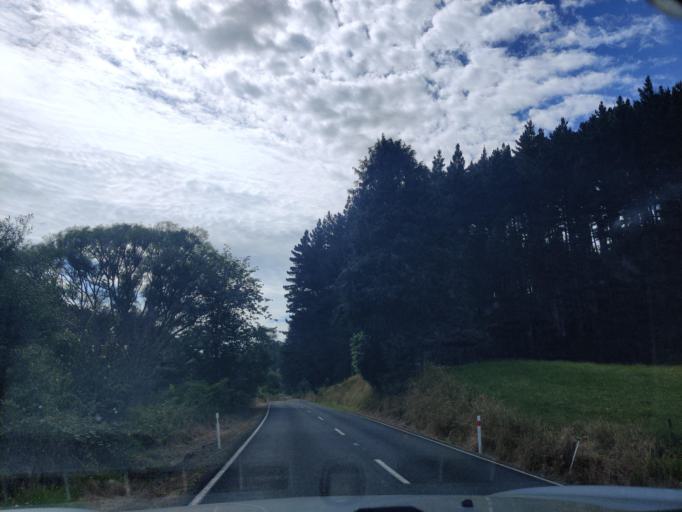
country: NZ
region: Waikato
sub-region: Otorohanga District
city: Otorohanga
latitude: -38.0952
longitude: 175.1121
